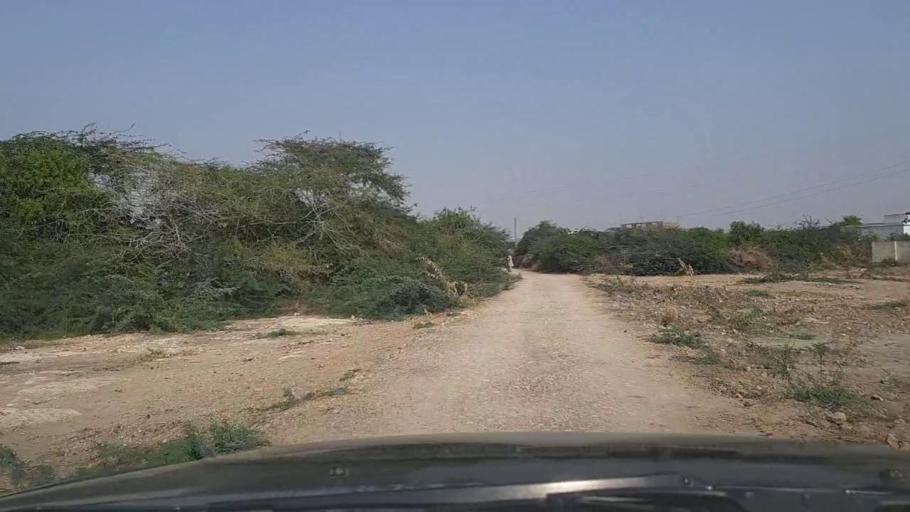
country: PK
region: Sindh
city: Thatta
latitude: 24.8032
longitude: 67.9078
